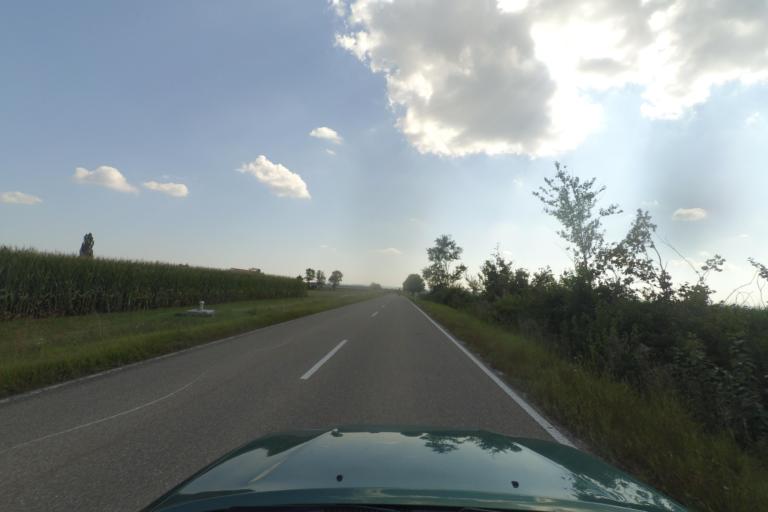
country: DE
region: Bavaria
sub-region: Swabia
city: Munningen
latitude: 48.9136
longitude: 10.6045
